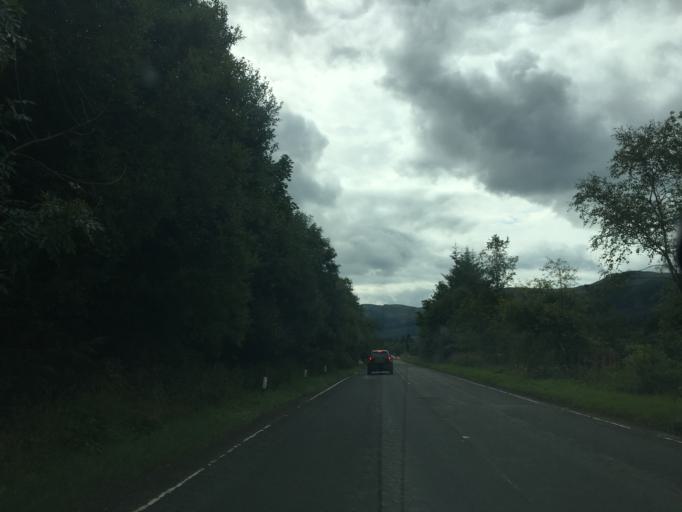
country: GB
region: Scotland
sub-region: Stirling
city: Callander
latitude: 56.3339
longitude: -4.3240
